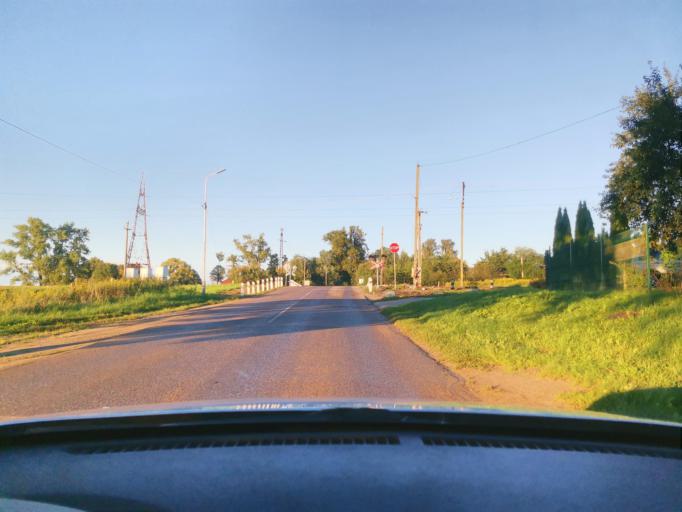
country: RU
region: Kaliningrad
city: Chernyakhovsk
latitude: 54.6571
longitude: 21.8271
